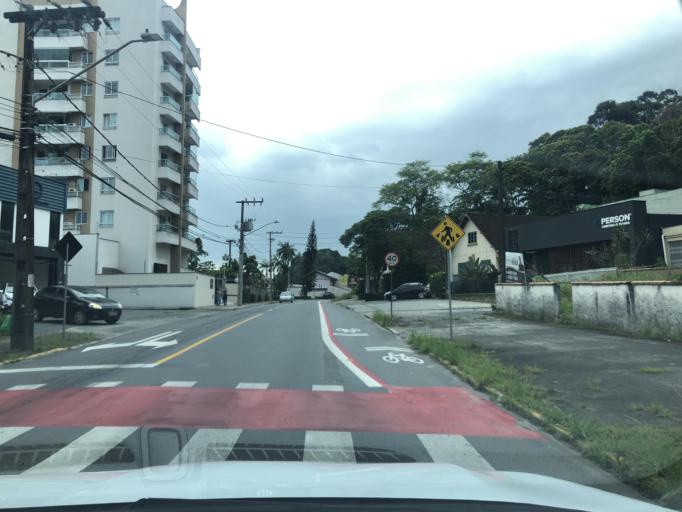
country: BR
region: Santa Catarina
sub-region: Joinville
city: Joinville
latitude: -26.3215
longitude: -48.8596
